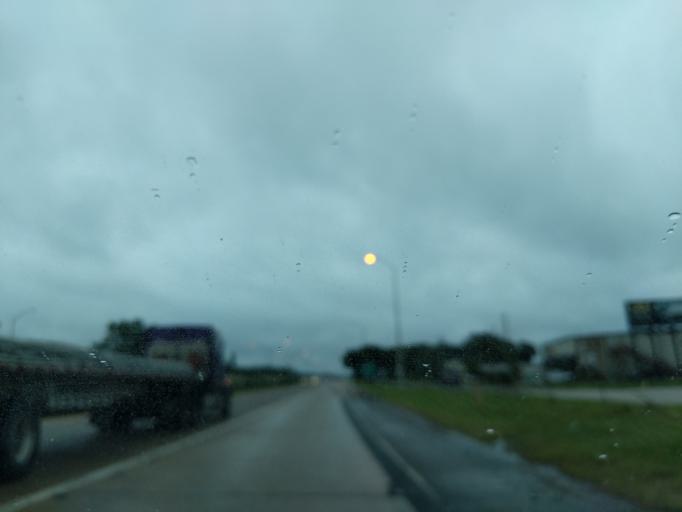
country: US
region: Louisiana
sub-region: Bossier Parish
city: Bossier City
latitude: 32.5293
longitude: -93.6705
